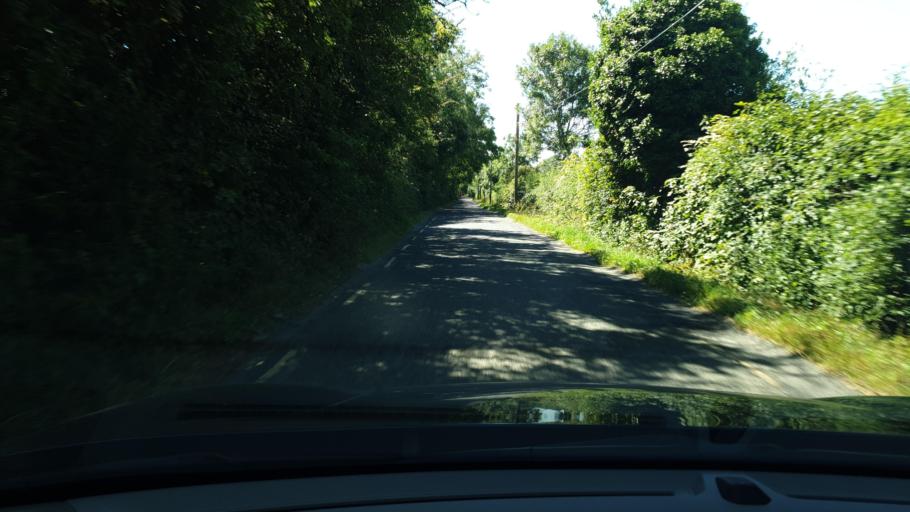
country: IE
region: Leinster
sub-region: An Mhi
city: Dunboyne
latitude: 53.3850
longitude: -6.4705
